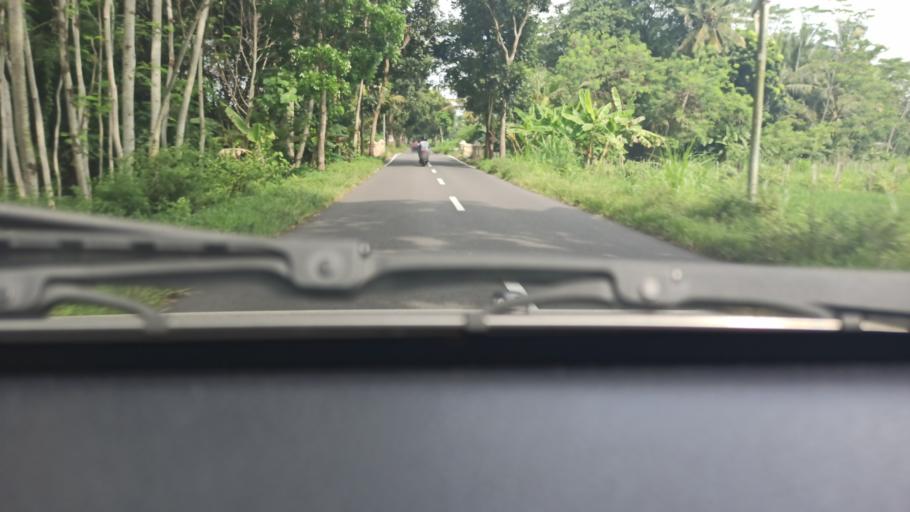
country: ID
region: Daerah Istimewa Yogyakarta
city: Sleman
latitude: -7.6904
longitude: 110.2987
